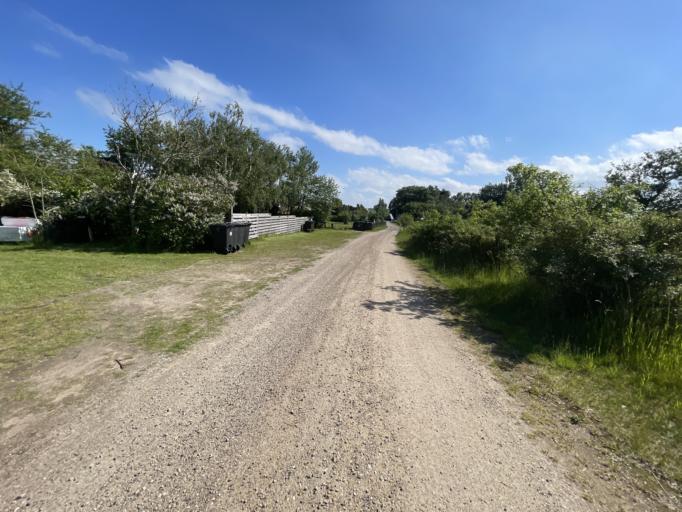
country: DK
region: Zealand
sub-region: Lejre Kommune
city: Ejby
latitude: 55.7933
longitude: 11.8317
